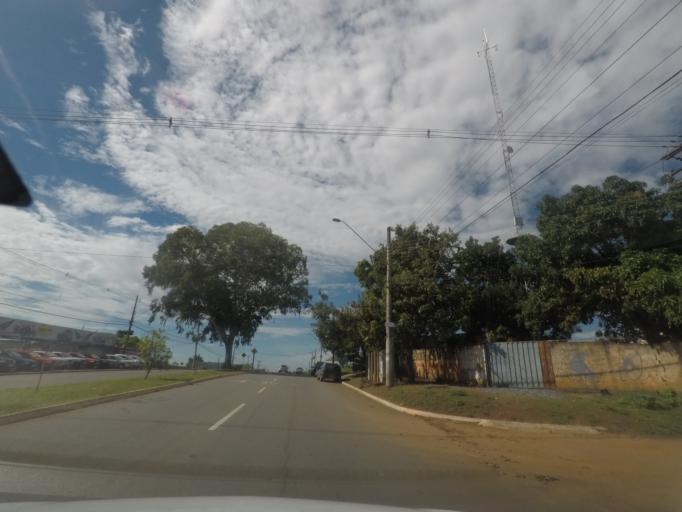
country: BR
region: Goias
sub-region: Aparecida De Goiania
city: Aparecida de Goiania
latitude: -16.8083
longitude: -49.2814
